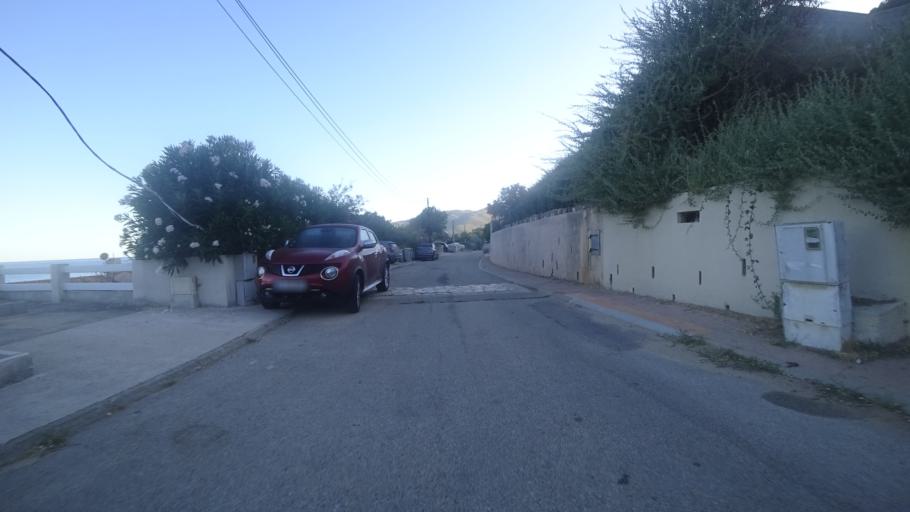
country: FR
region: Corsica
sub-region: Departement de la Corse-du-Sud
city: Alata
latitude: 41.9778
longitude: 8.6664
